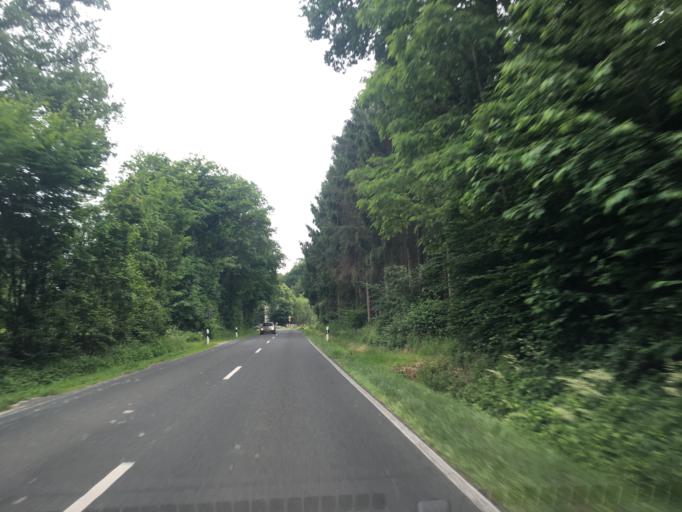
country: DE
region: North Rhine-Westphalia
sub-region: Regierungsbezirk Munster
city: Laer
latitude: 52.0886
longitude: 7.3449
